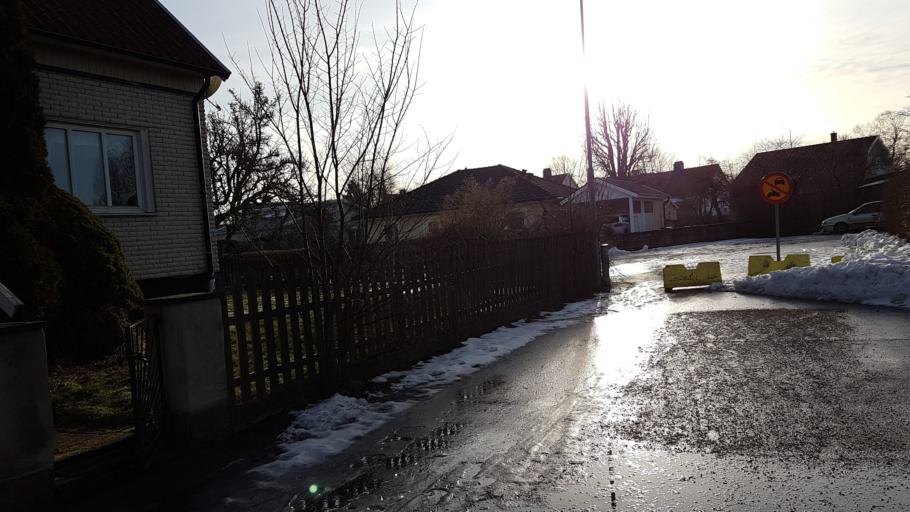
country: SE
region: Gotland
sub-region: Gotland
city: Visby
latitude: 57.6334
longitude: 18.3143
